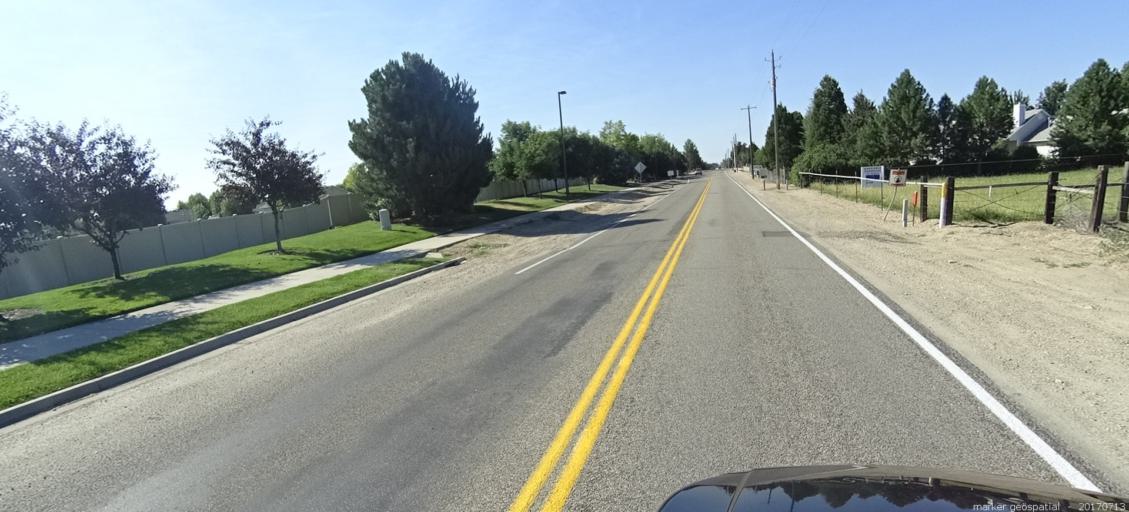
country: US
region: Idaho
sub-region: Ada County
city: Kuna
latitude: 43.5160
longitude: -116.4139
